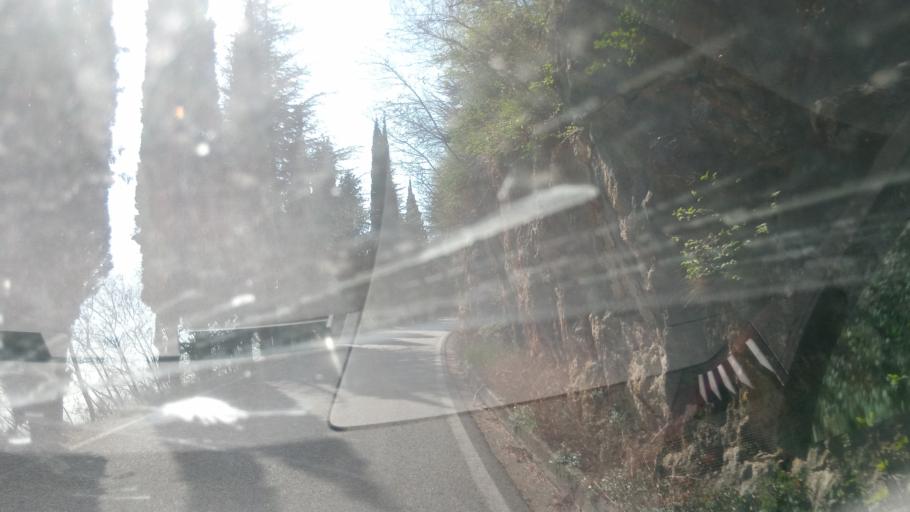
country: IT
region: Veneto
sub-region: Provincia di Treviso
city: Borso del Grappa
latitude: 45.8140
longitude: 11.7658
